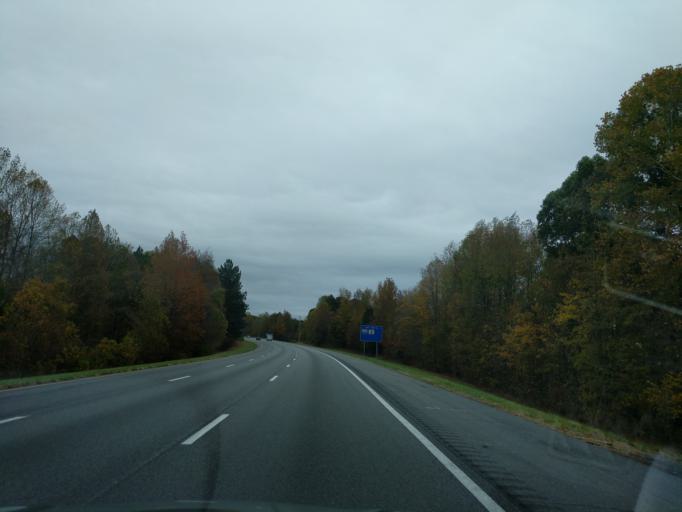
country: US
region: North Carolina
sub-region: Davidson County
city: Lexington
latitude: 35.8037
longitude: -80.1906
